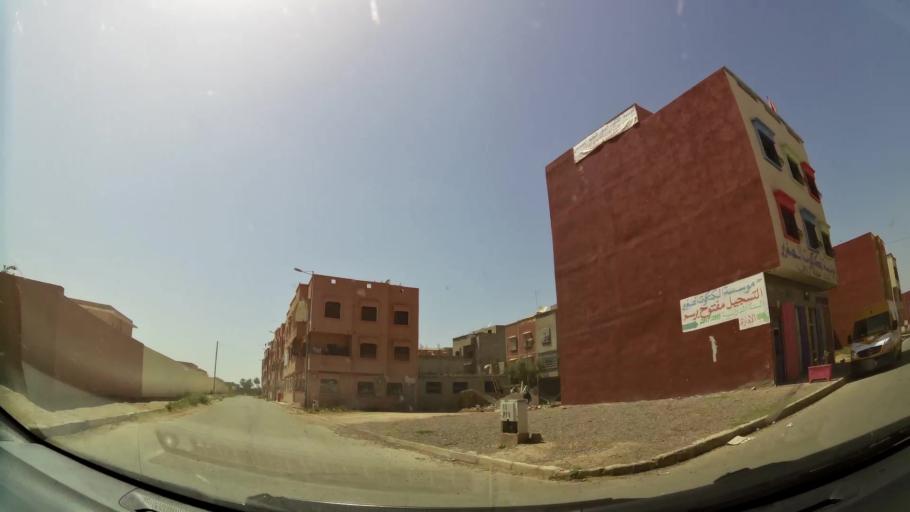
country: MA
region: Souss-Massa-Draa
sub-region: Inezgane-Ait Mellou
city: Inezgane
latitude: 30.3442
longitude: -9.5174
